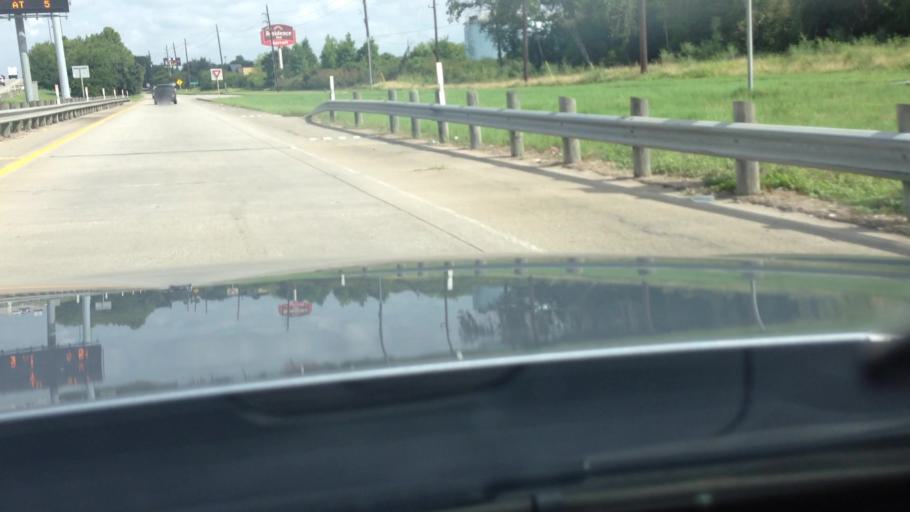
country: US
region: Texas
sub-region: Harris County
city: Hudson
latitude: 29.9509
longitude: -95.5340
